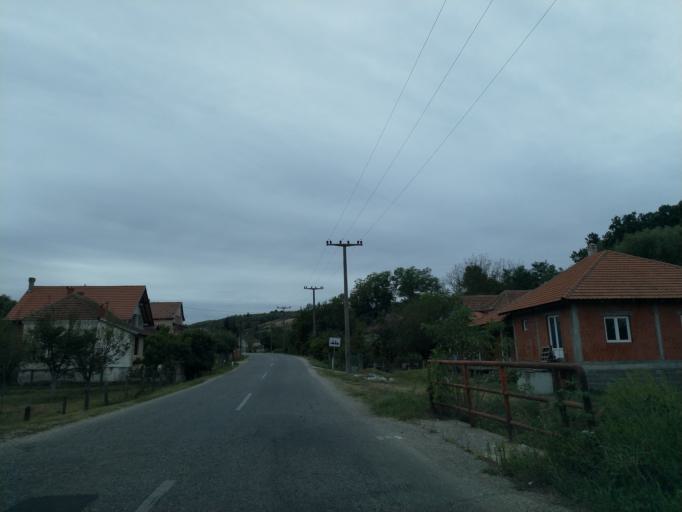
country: RS
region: Central Serbia
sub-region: Pomoravski Okrug
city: Jagodina
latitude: 44.0589
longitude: 21.1818
